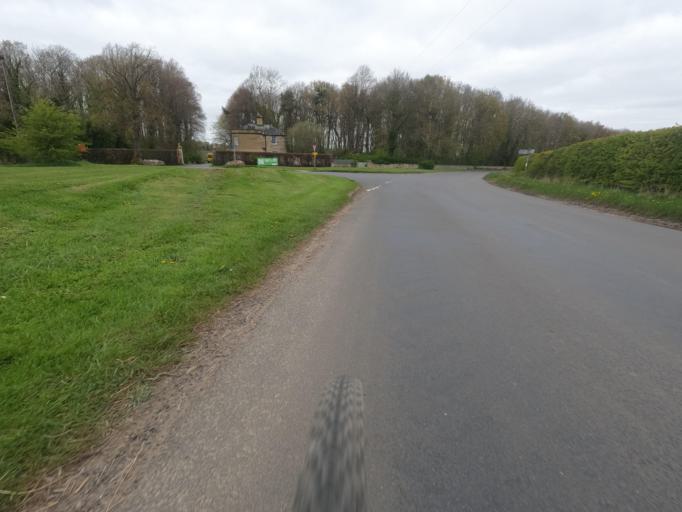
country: GB
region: England
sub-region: Northumberland
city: Ponteland
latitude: 55.0834
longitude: -1.7639
